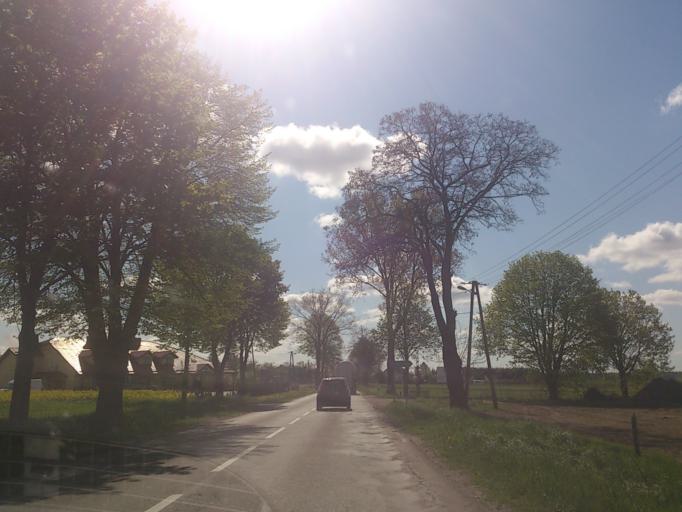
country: PL
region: Warmian-Masurian Voivodeship
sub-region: Powiat dzialdowski
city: Ilowo -Osada
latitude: 53.2010
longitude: 20.2454
